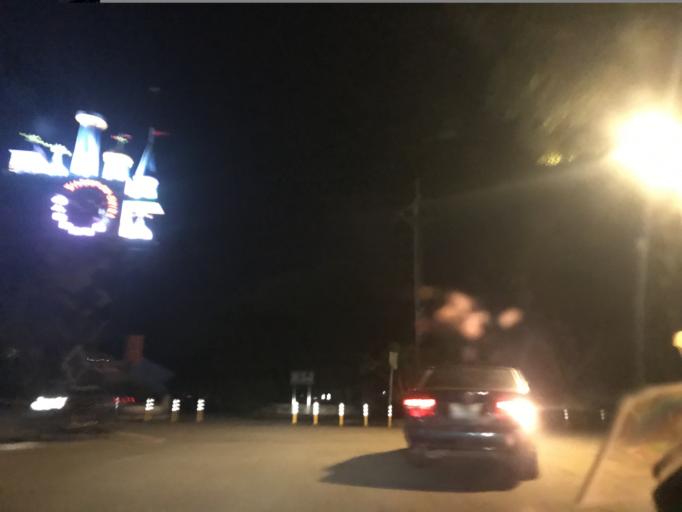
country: TW
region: Taiwan
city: Daxi
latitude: 24.8320
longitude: 121.1890
